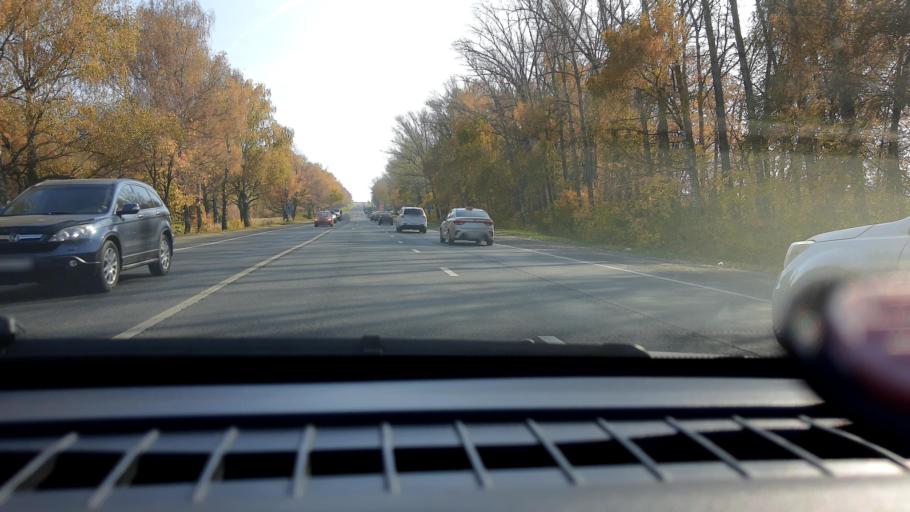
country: RU
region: Nizjnij Novgorod
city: Kstovo
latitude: 56.1395
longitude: 44.2318
